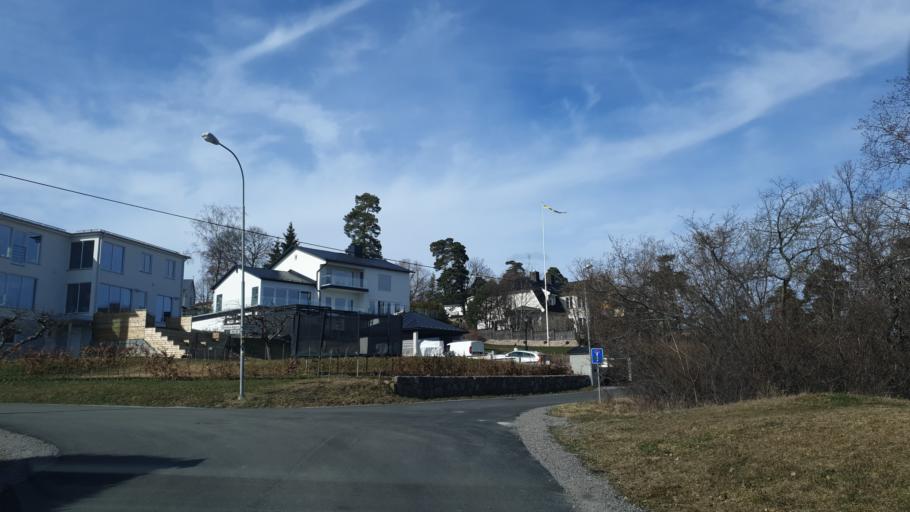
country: SE
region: Stockholm
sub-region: Sollentuna Kommun
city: Sollentuna
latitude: 59.4201
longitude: 17.9819
